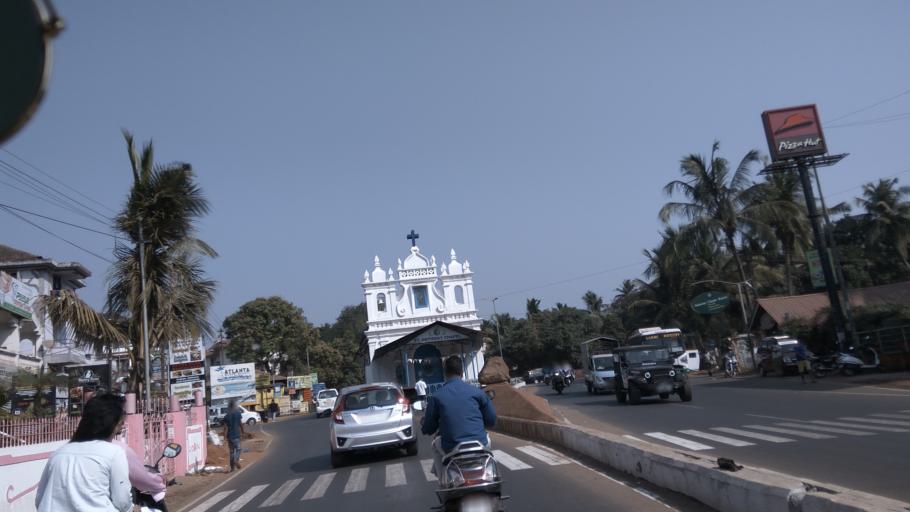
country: IN
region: Goa
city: Calangute
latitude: 15.5361
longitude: 73.7643
